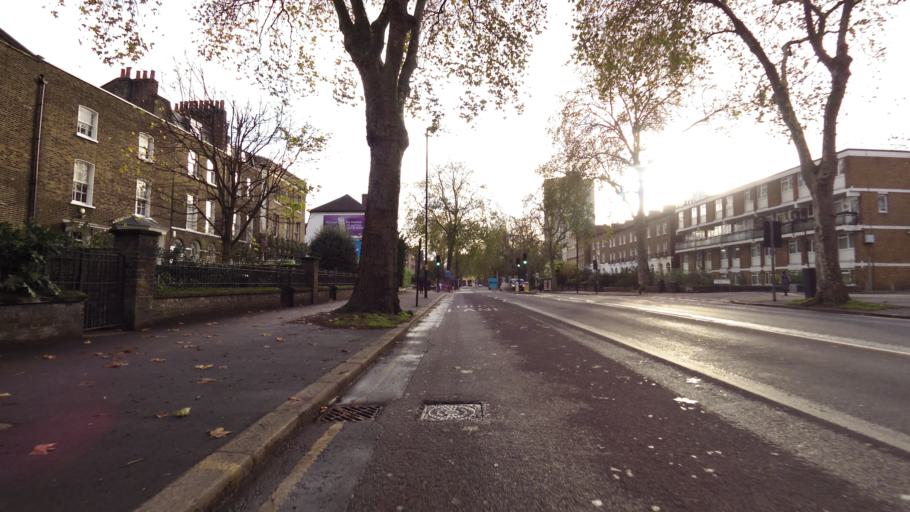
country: GB
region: England
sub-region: Greater London
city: Lambeth
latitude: 51.4936
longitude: -0.1108
